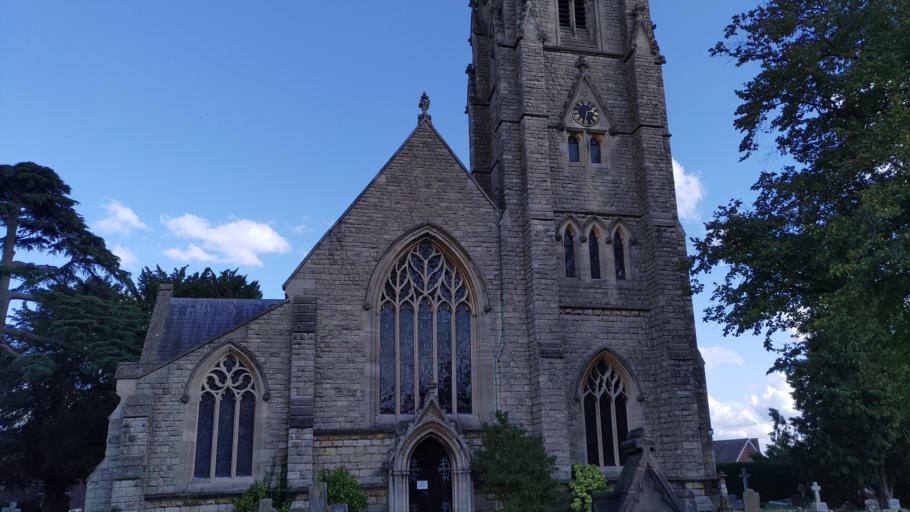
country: GB
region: England
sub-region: Hertfordshire
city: Potters Bar
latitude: 51.7051
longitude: -0.1506
